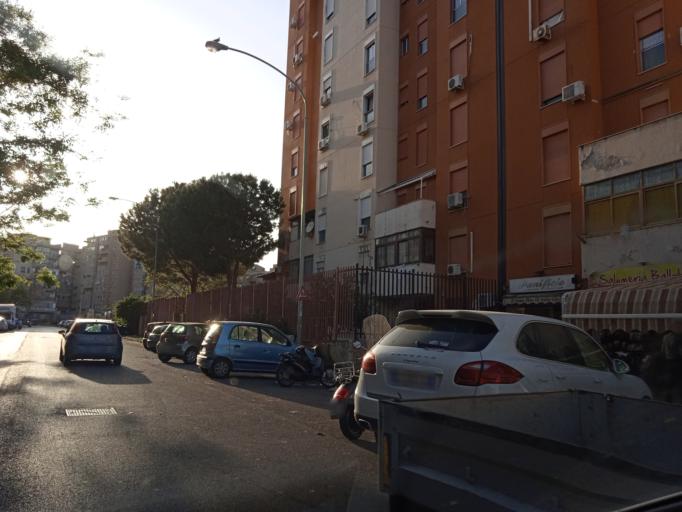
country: IT
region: Sicily
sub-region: Palermo
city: Ciaculli
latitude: 38.0851
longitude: 13.3652
